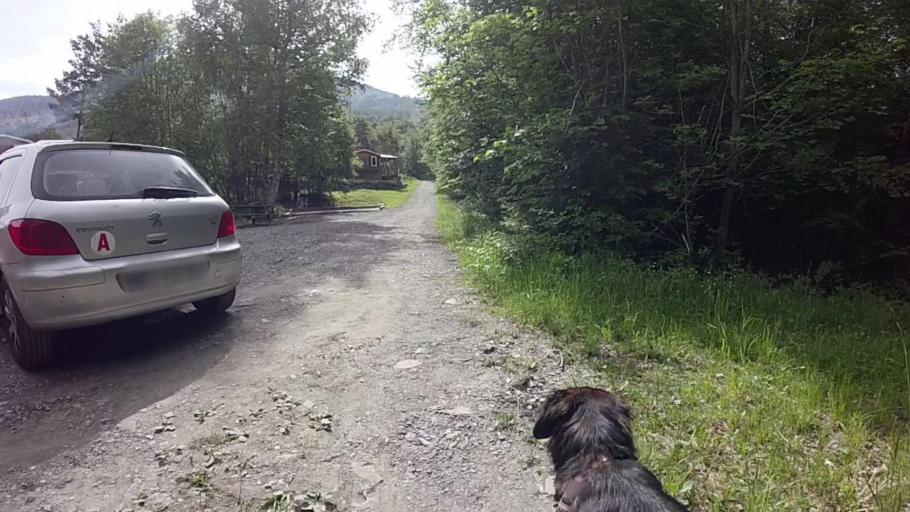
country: FR
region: Provence-Alpes-Cote d'Azur
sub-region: Departement des Alpes-de-Haute-Provence
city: Seyne-les-Alpes
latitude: 44.4092
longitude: 6.3448
